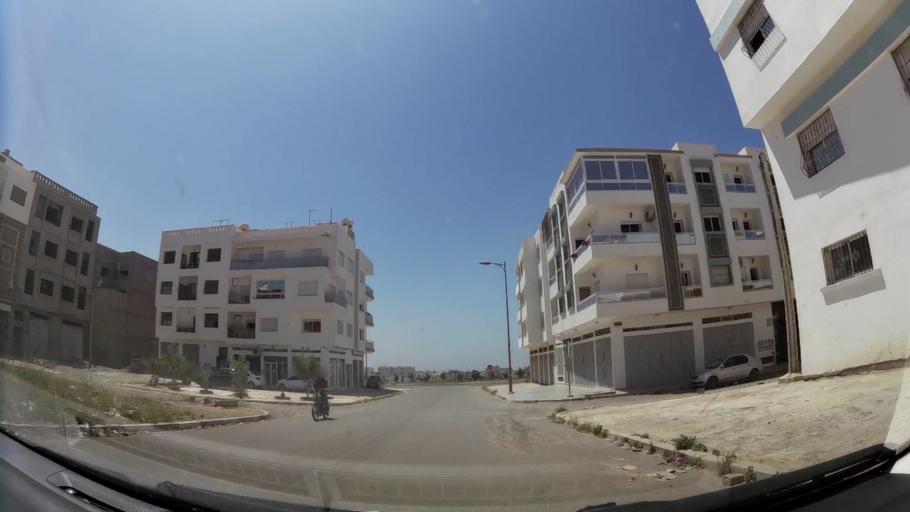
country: MA
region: Oued ed Dahab-Lagouira
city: Dakhla
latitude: 30.4288
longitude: -9.5597
